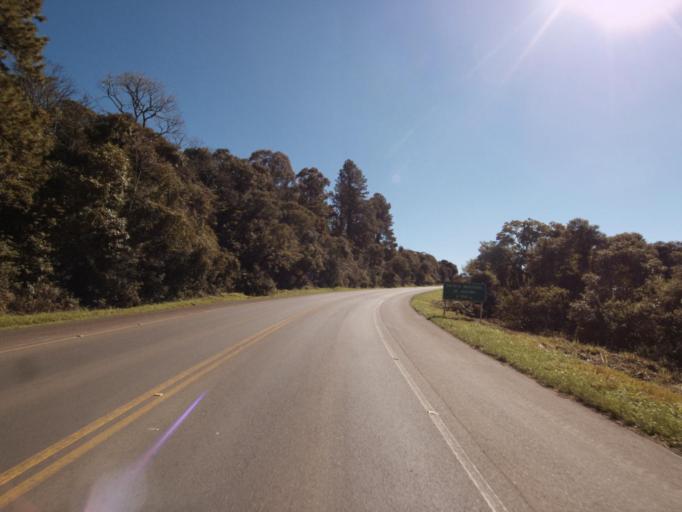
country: BR
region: Santa Catarina
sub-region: Joacaba
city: Joacaba
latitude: -27.1555
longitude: -51.6015
